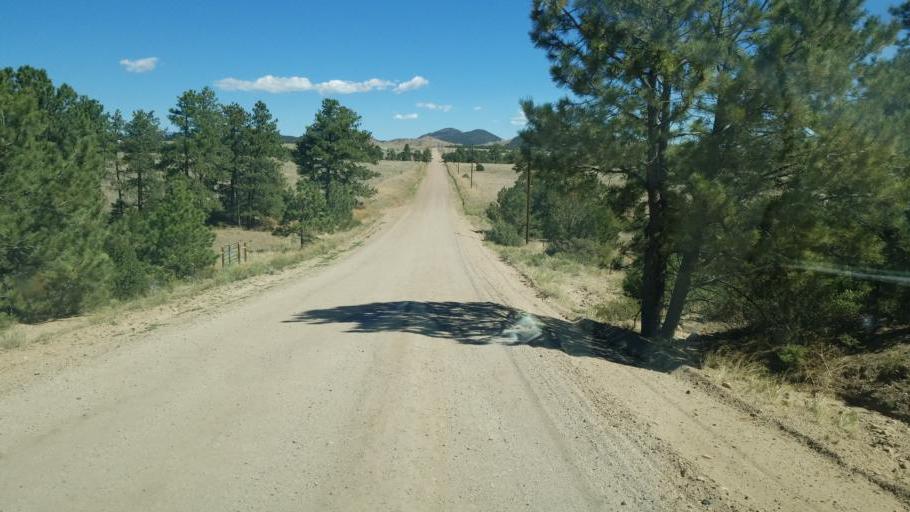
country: US
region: Colorado
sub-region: Custer County
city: Westcliffe
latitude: 38.2709
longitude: -105.5010
